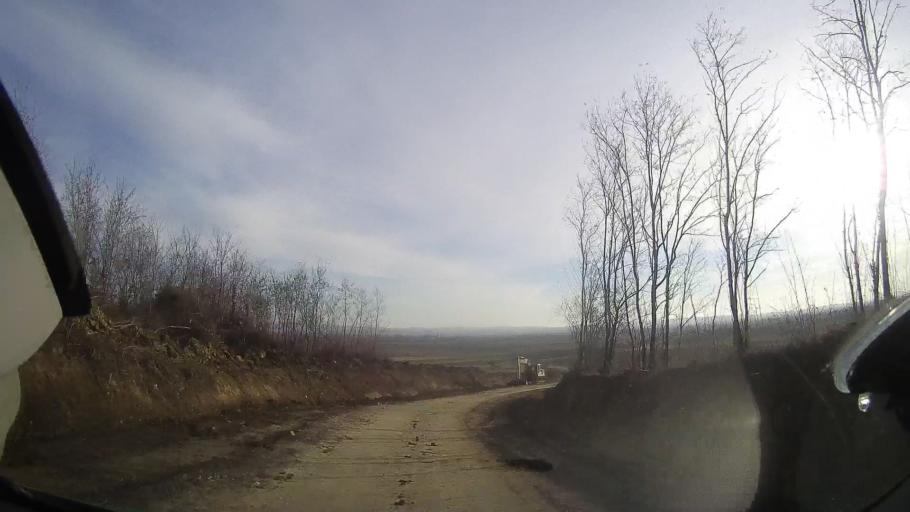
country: RO
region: Bihor
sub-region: Comuna Tileagd
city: Tileagd
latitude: 47.0952
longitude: 22.1776
